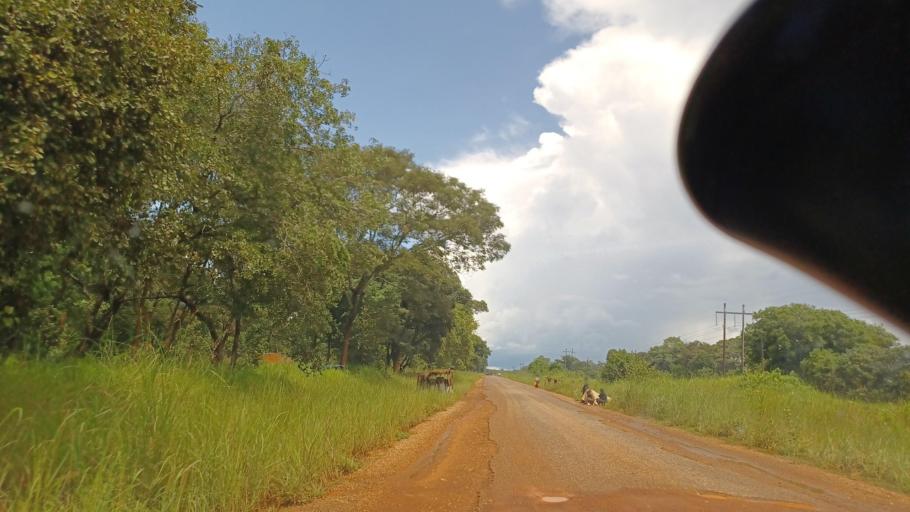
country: ZM
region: North-Western
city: Kasempa
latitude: -12.8970
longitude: 26.0537
